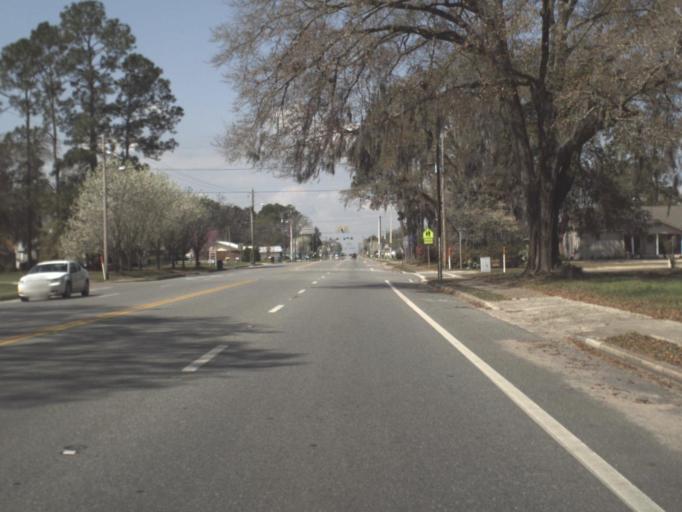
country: US
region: Florida
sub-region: Liberty County
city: Bristol
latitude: 30.4319
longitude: -84.9728
